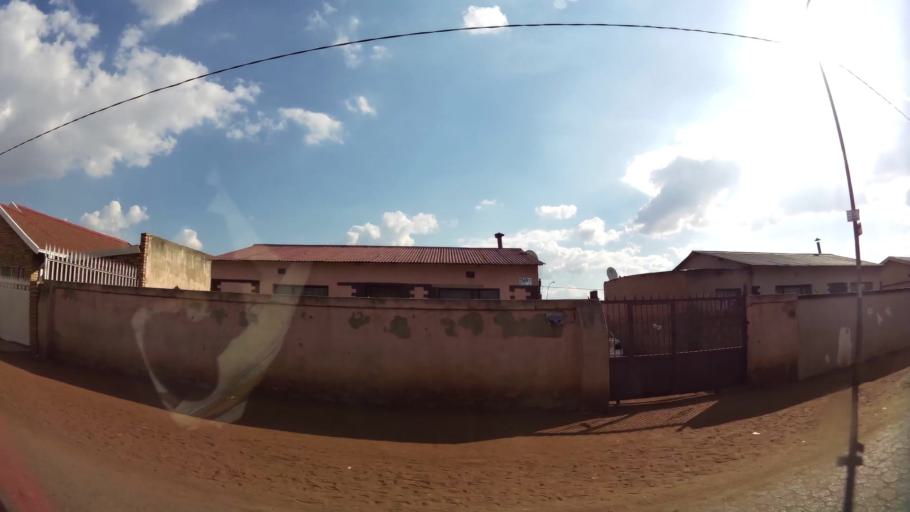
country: ZA
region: Gauteng
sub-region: City of Johannesburg Metropolitan Municipality
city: Soweto
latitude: -26.2228
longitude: 27.8599
